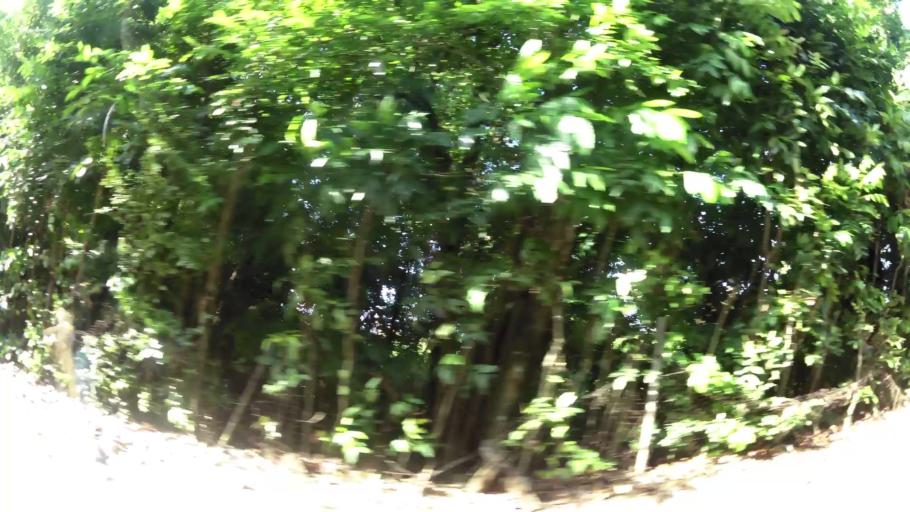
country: MQ
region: Martinique
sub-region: Martinique
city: Le Lamentin
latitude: 14.6256
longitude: -61.0251
